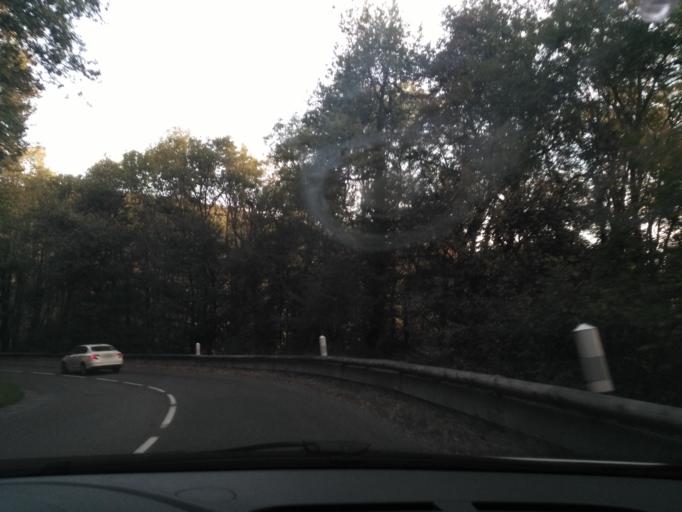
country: FR
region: Rhone-Alpes
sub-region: Departement du Rhone
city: Limonest
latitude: 45.8480
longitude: 4.7923
